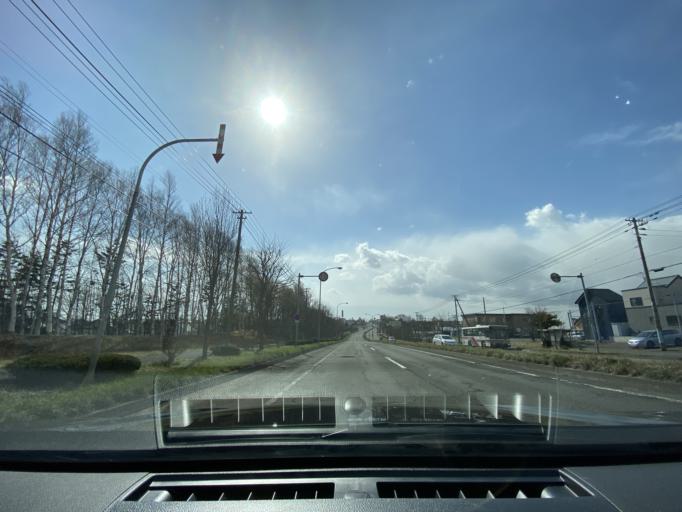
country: JP
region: Hokkaido
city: Kitahiroshima
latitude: 42.9693
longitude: 141.4812
